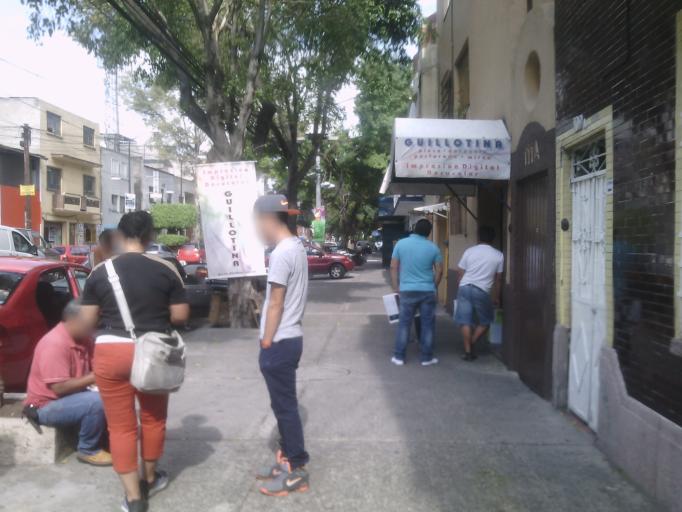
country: MX
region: Mexico City
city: Benito Juarez
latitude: 19.4083
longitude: -99.1388
